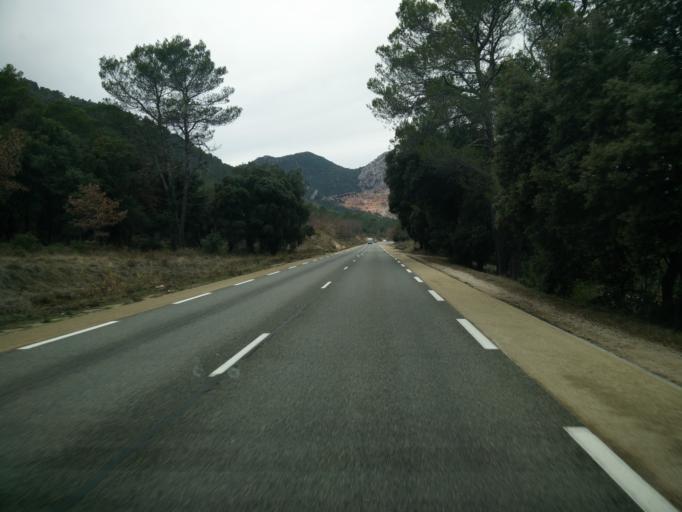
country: FR
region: Provence-Alpes-Cote d'Azur
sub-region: Departement du Var
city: Brignoles
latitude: 43.3802
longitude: 6.0646
